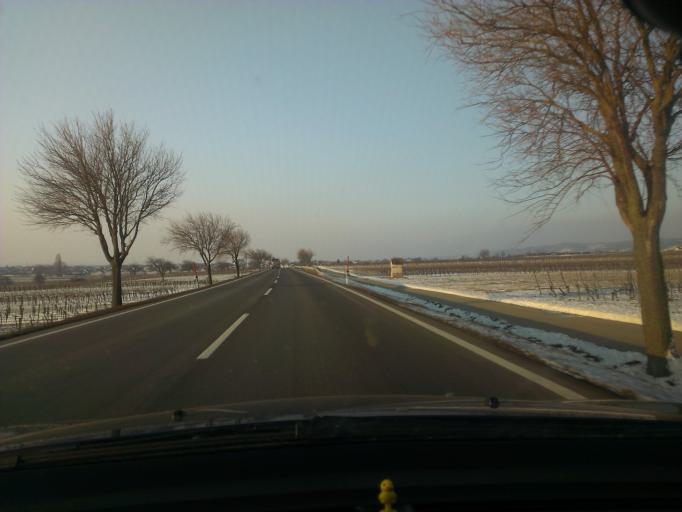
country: AT
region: Burgenland
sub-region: Eisenstadt-Umgebung
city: Breitenbrunn
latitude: 47.9231
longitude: 16.7070
